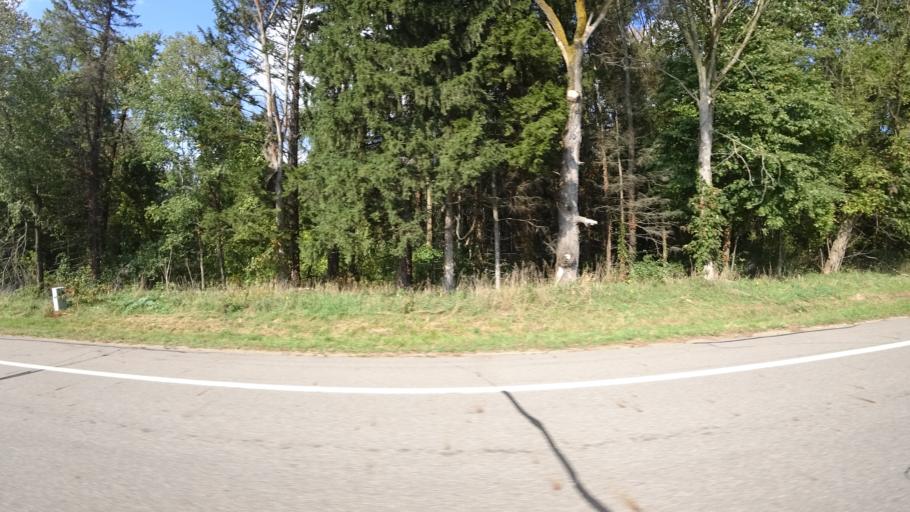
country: US
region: Michigan
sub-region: Saint Joseph County
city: Colon
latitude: 42.0101
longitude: -85.4106
